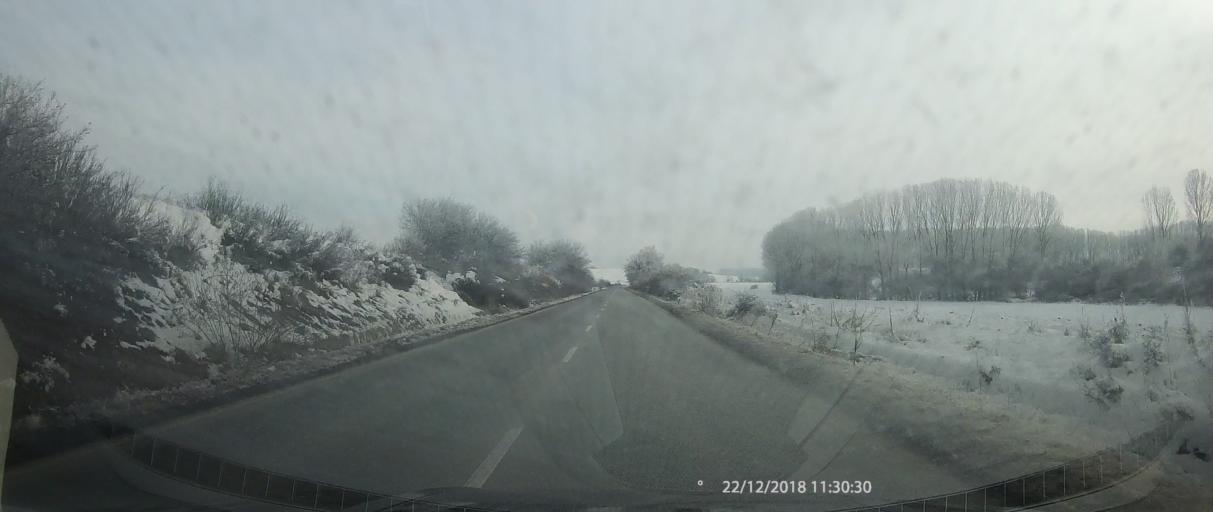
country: BG
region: Kyustendil
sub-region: Obshtina Bobovdol
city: Bobovdol
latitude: 42.2732
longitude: 22.9728
